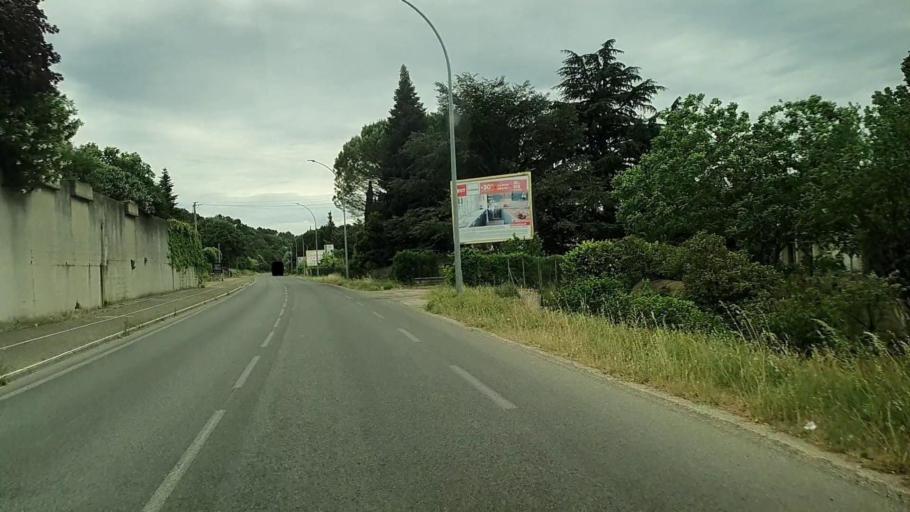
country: FR
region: Languedoc-Roussillon
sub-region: Departement du Gard
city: Bagnols-sur-Ceze
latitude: 44.1521
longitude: 4.6128
